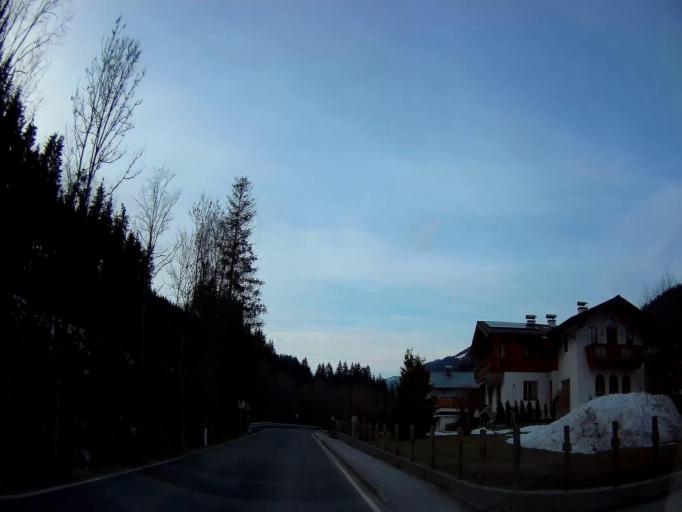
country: AT
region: Salzburg
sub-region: Politischer Bezirk Hallein
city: Abtenau
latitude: 47.5290
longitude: 13.4256
